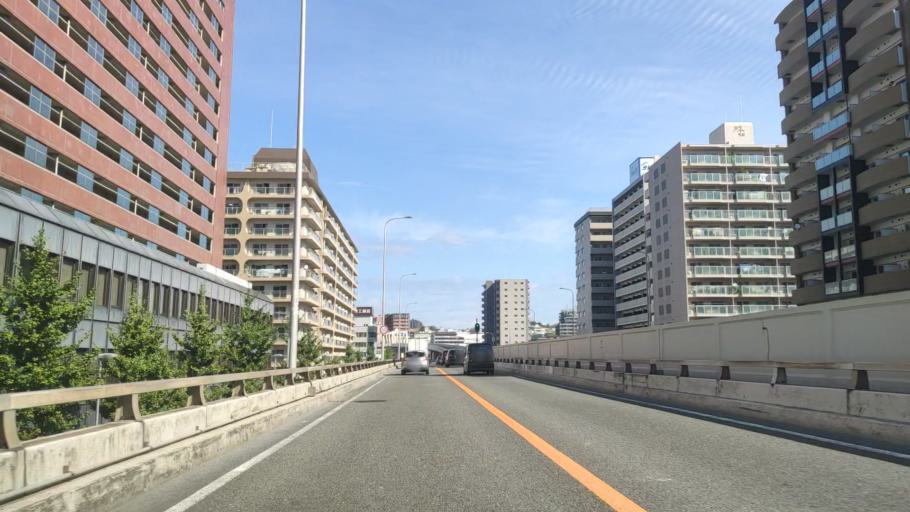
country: JP
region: Osaka
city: Suita
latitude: 34.7625
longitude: 135.4972
